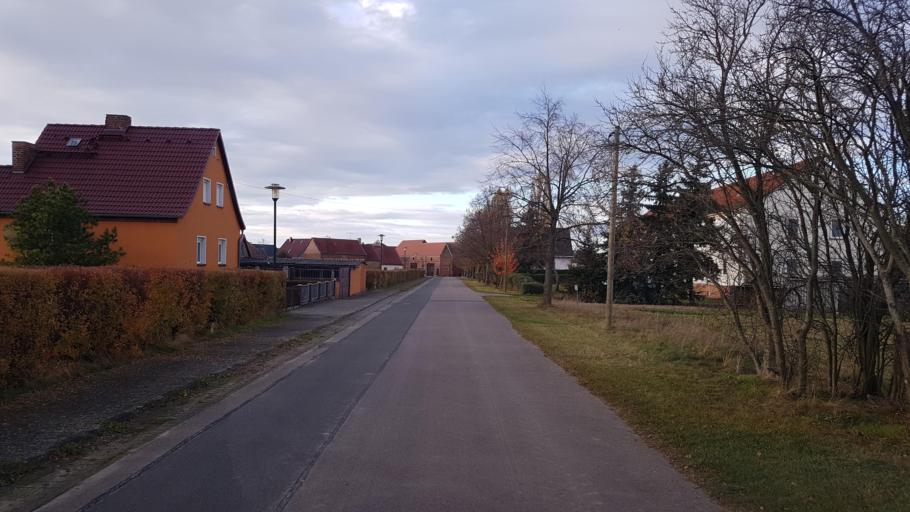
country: DE
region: Saxony-Anhalt
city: Zahna
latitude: 51.9463
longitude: 12.8430
